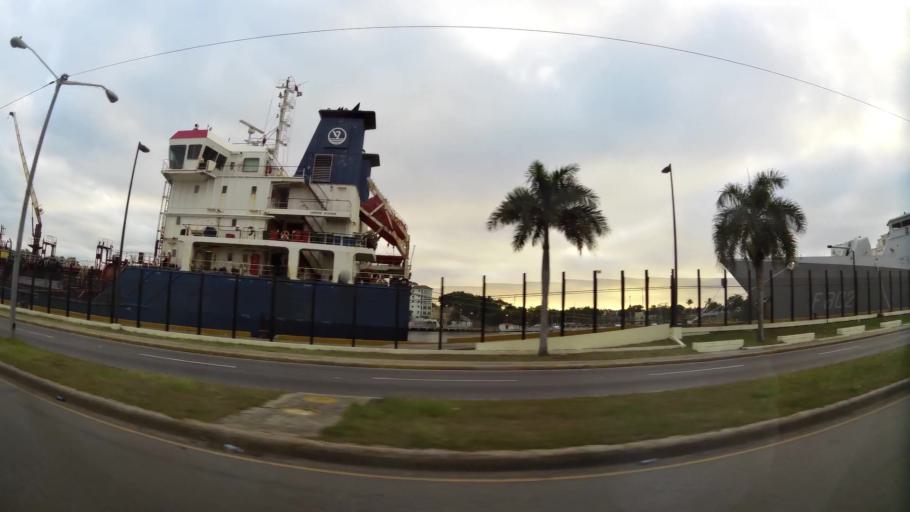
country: DO
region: Nacional
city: San Carlos
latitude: 18.4779
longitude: -69.8822
